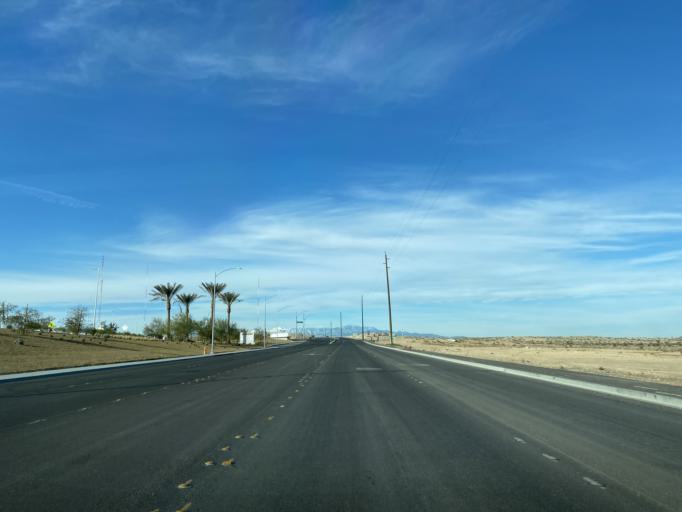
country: US
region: Nevada
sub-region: Clark County
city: Nellis Air Force Base
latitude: 36.2697
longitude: -115.0407
